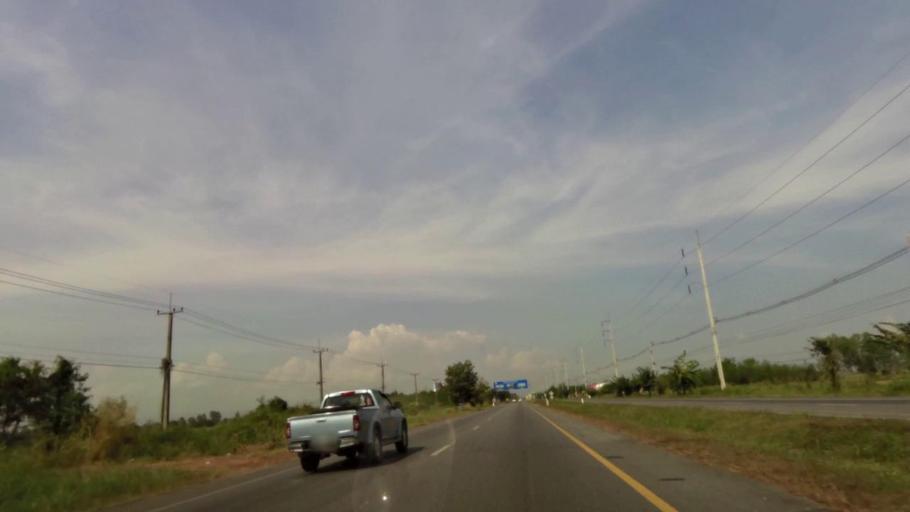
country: TH
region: Uttaradit
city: Uttaradit
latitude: 17.5689
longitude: 100.1544
